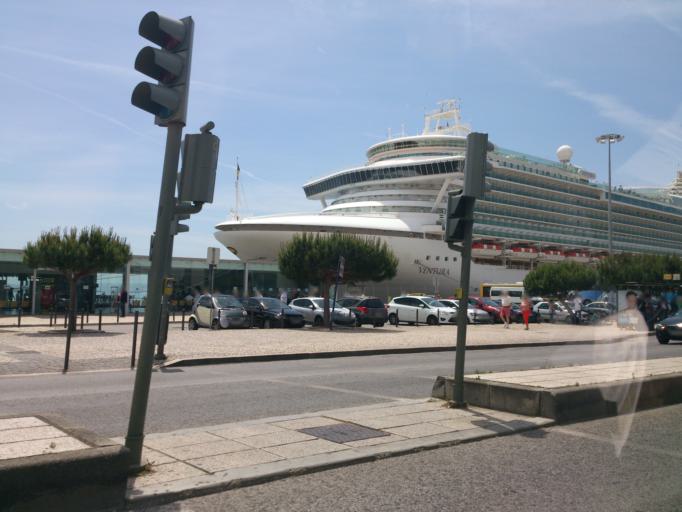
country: PT
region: Lisbon
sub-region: Lisbon
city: Lisbon
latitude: 38.7133
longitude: -9.1229
